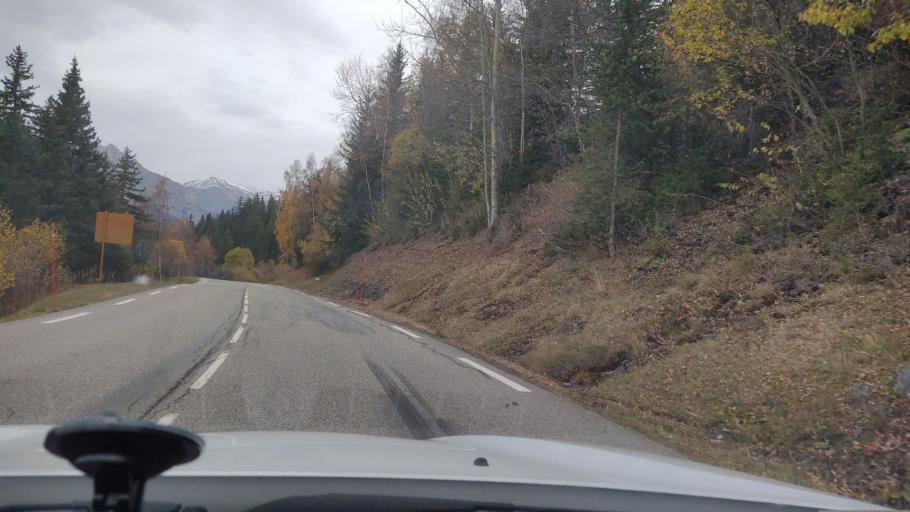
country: FR
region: Rhone-Alpes
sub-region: Departement de la Savoie
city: Bourg-Saint-Maurice
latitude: 45.5813
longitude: 6.7885
